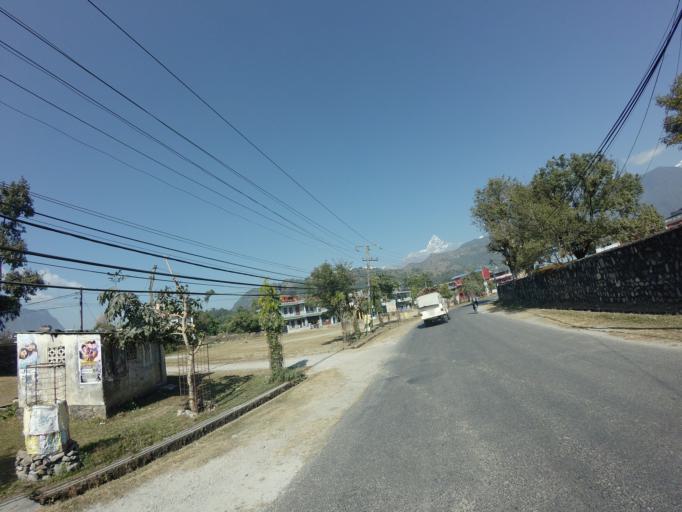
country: NP
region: Western Region
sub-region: Gandaki Zone
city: Pokhara
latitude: 28.2622
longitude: 83.9794
